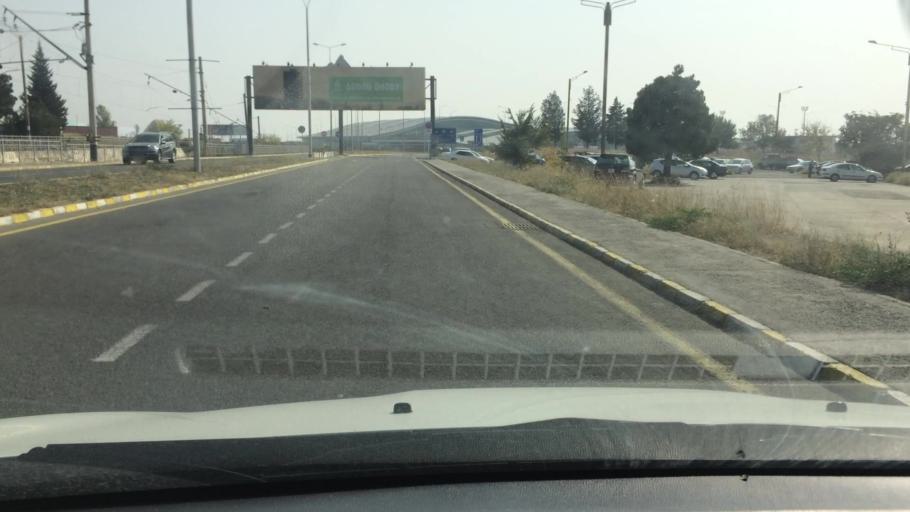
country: GE
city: Didi Lilo
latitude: 41.6737
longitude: 44.9621
